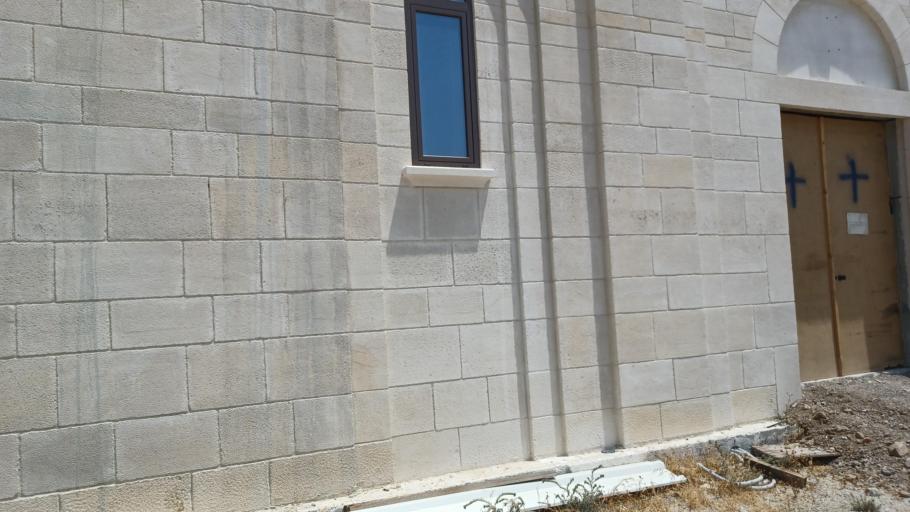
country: CY
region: Larnaka
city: Troulloi
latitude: 35.0275
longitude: 33.5946
